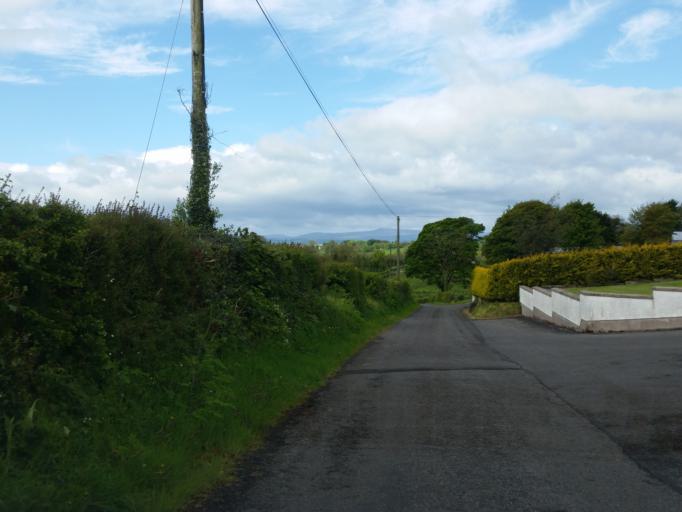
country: GB
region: Northern Ireland
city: Lisnaskea
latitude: 54.2568
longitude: -7.4011
